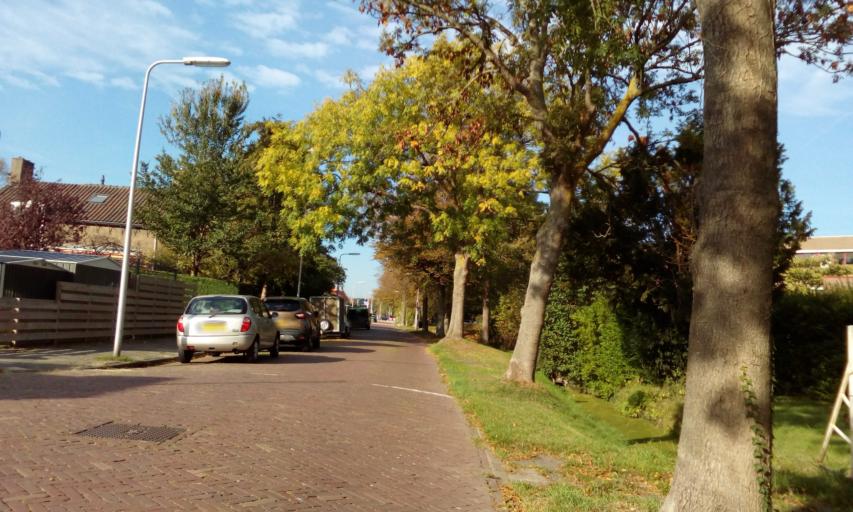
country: NL
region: South Holland
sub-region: Gemeente Westland
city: Naaldwijk
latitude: 51.9896
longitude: 4.2178
